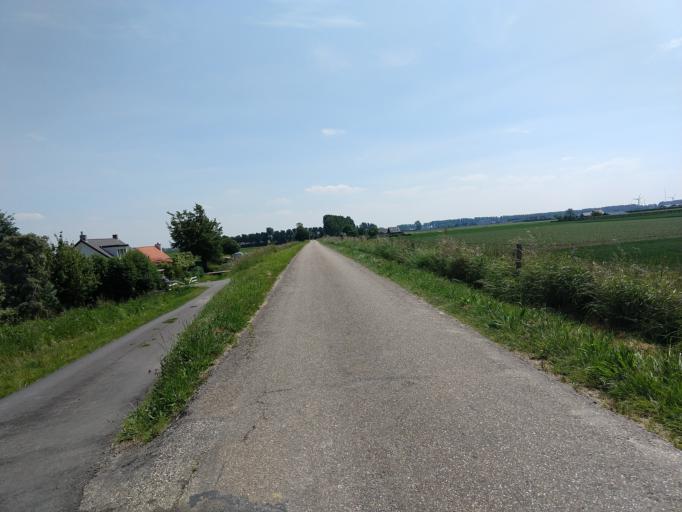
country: NL
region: Zeeland
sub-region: Gemeente Borsele
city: Borssele
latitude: 51.4718
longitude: 3.7607
